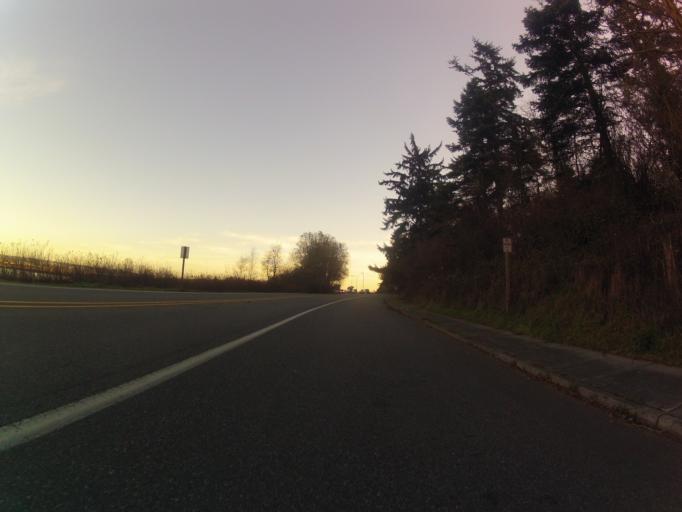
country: US
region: Washington
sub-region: Island County
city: Coupeville
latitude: 48.1618
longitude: -122.6750
